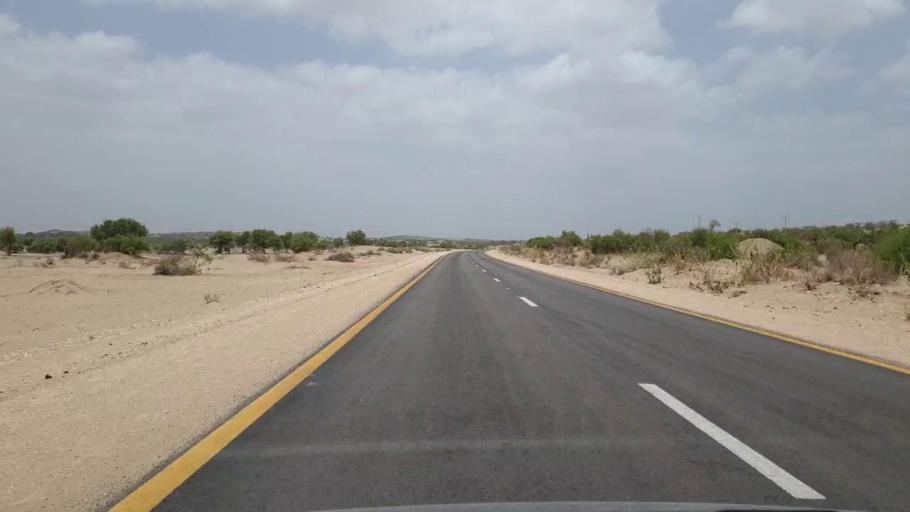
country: PK
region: Sindh
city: Naukot
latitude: 24.8447
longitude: 69.5421
